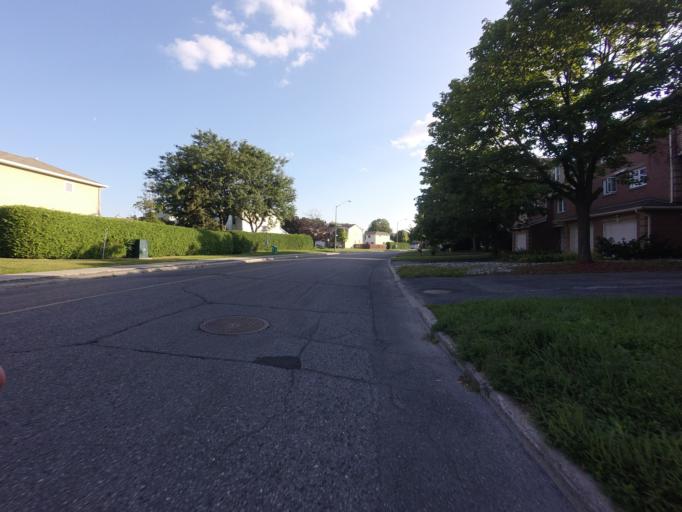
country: CA
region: Ontario
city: Bells Corners
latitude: 45.3393
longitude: -75.7619
